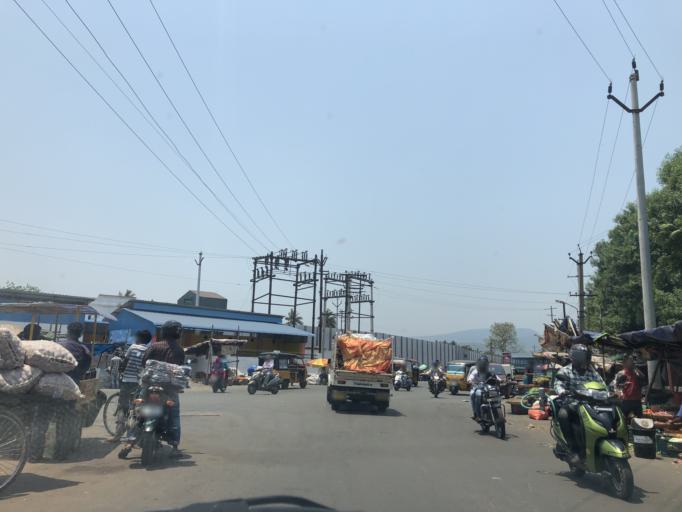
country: IN
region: Andhra Pradesh
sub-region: Vishakhapatnam
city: Yarada
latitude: 17.7105
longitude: 83.2944
